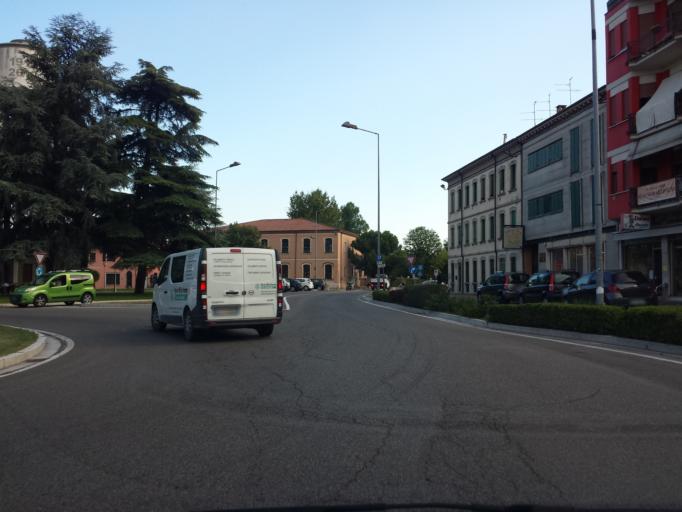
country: IT
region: Veneto
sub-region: Provincia di Verona
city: San Giovanni Lupatoto
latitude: 45.3820
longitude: 11.0446
